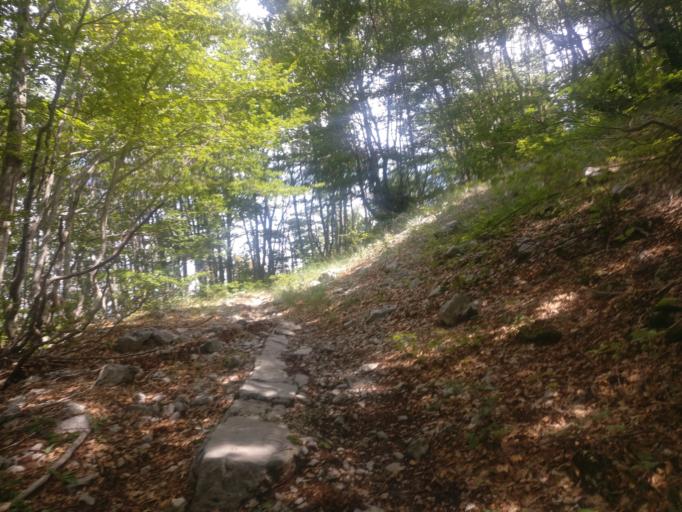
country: ME
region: Kotor
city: Kotor
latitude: 42.4067
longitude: 18.8395
